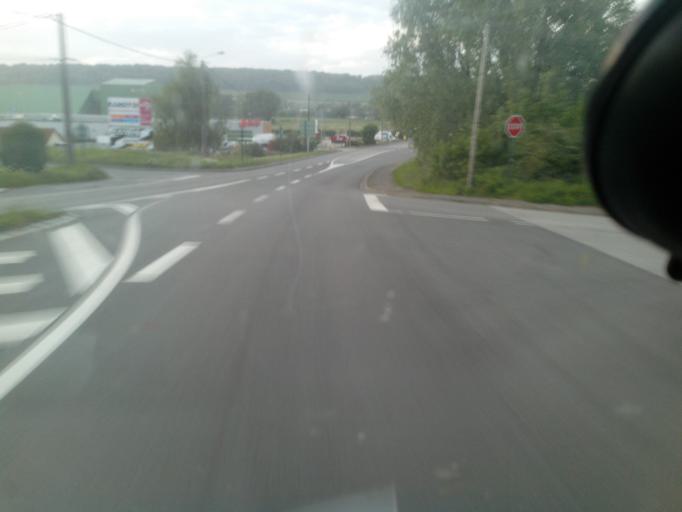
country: FR
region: Nord-Pas-de-Calais
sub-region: Departement du Pas-de-Calais
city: Hesdin
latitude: 50.3695
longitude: 2.0287
